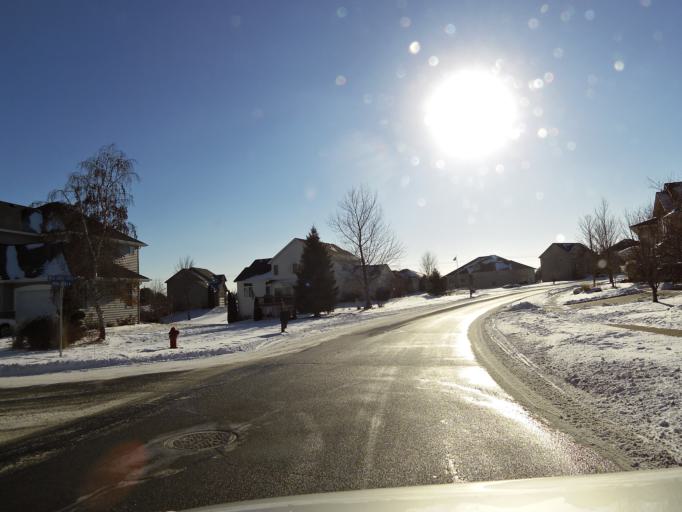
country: US
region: Minnesota
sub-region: Scott County
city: Prior Lake
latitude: 44.7266
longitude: -93.4572
